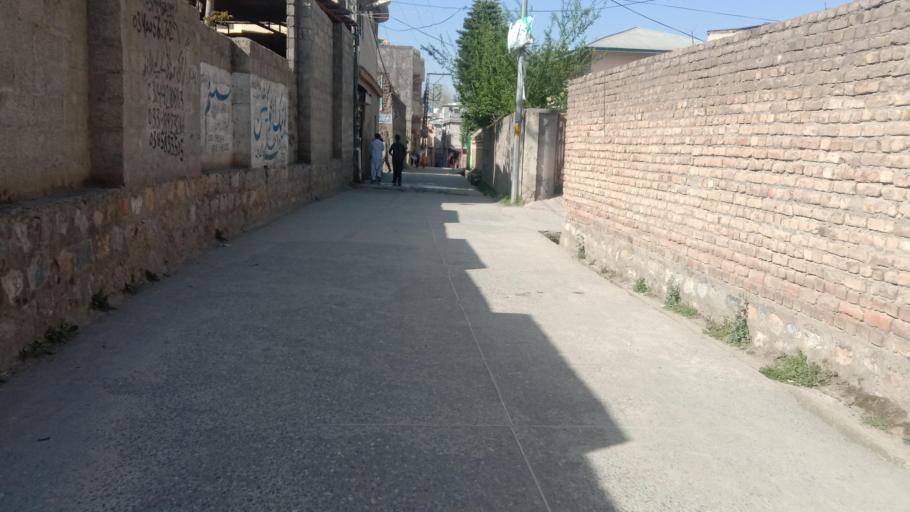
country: PK
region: Khyber Pakhtunkhwa
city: Abbottabad
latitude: 34.1765
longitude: 73.2249
